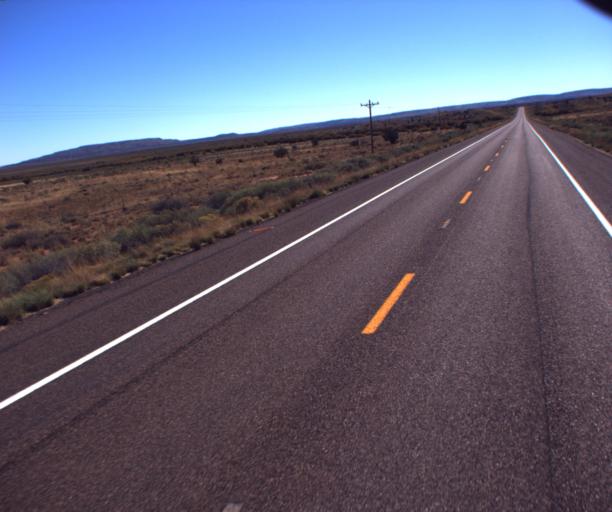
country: US
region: Arizona
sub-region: Apache County
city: Saint Johns
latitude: 34.6337
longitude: -109.6827
